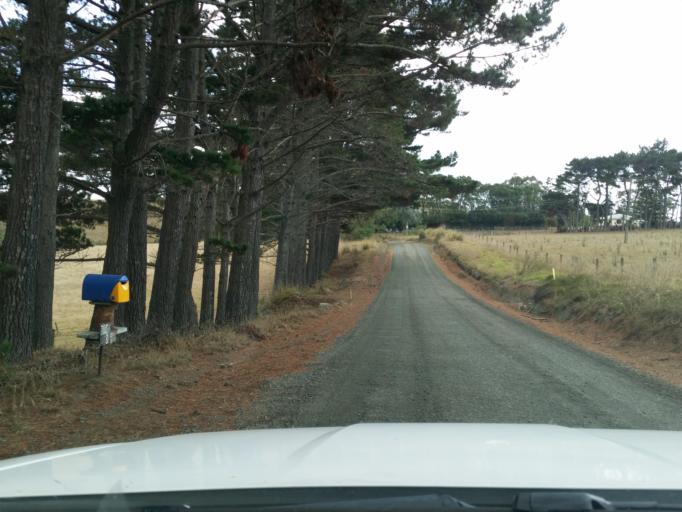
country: NZ
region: Auckland
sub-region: Auckland
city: Wellsford
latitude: -36.3276
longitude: 174.1422
